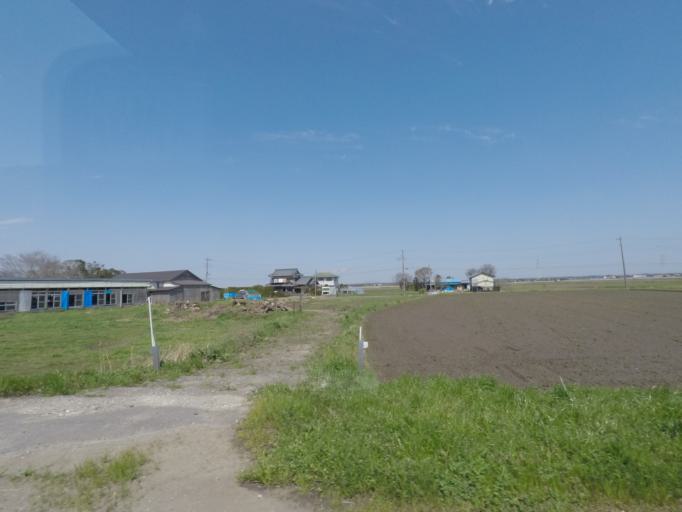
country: JP
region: Ibaraki
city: Edosaki
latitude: 35.8702
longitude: 140.3248
